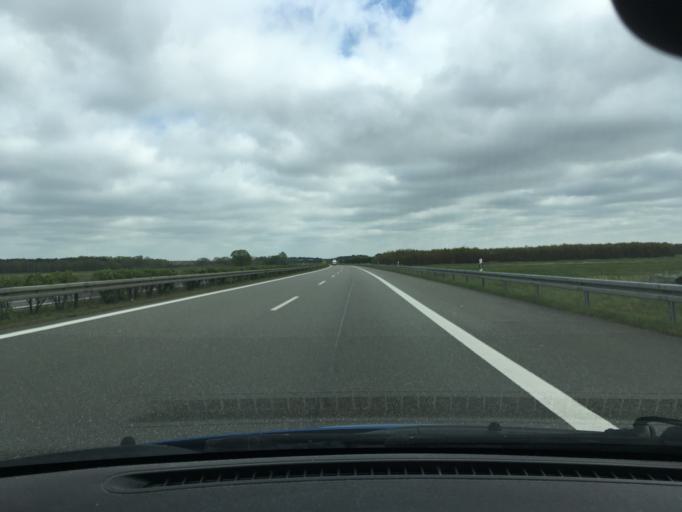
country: DE
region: Mecklenburg-Vorpommern
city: Sulstorf
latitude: 53.4736
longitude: 11.3067
